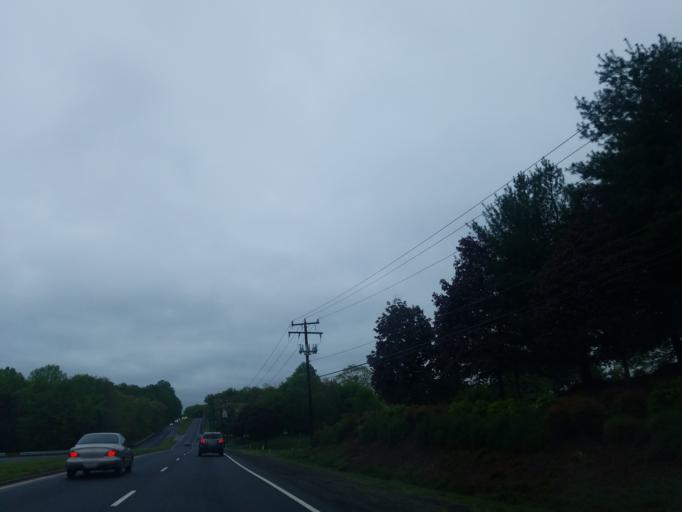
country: US
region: Virginia
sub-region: Fairfax County
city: Reston
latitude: 38.9748
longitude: -77.3203
